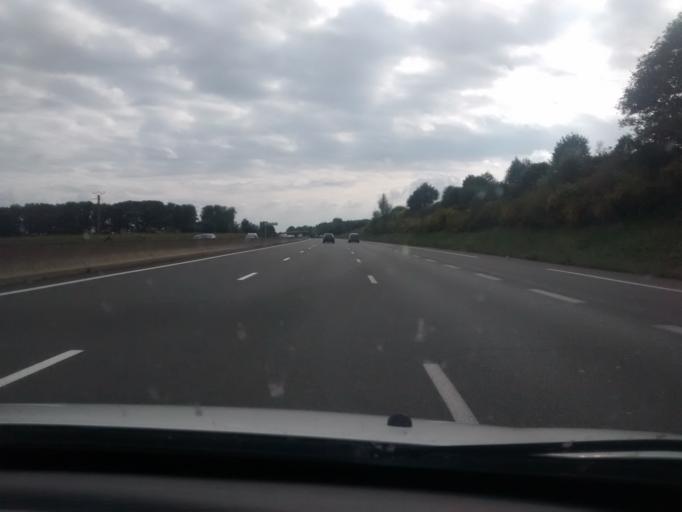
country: FR
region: Centre
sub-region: Departement d'Eure-et-Loir
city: Authon-du-Perche
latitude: 48.2127
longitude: 0.9387
